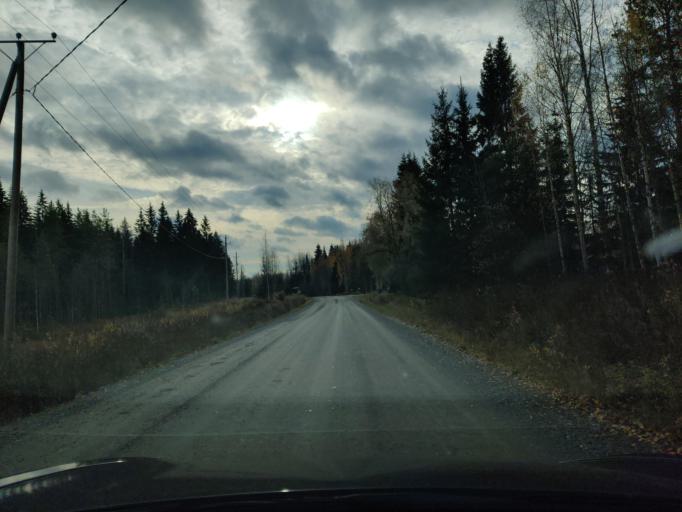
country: FI
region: Northern Savo
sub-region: Kuopio
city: Siilinjaervi
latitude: 63.1156
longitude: 27.5453
